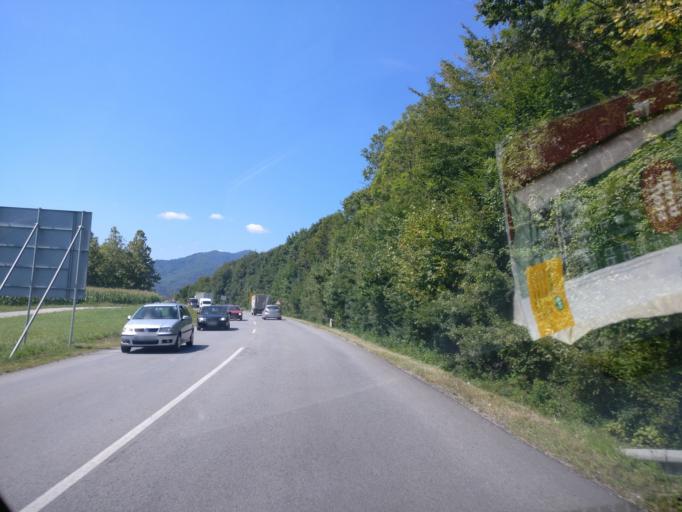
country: SI
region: Skofja Loka
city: Sv. Duh
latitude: 46.1694
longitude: 14.3440
